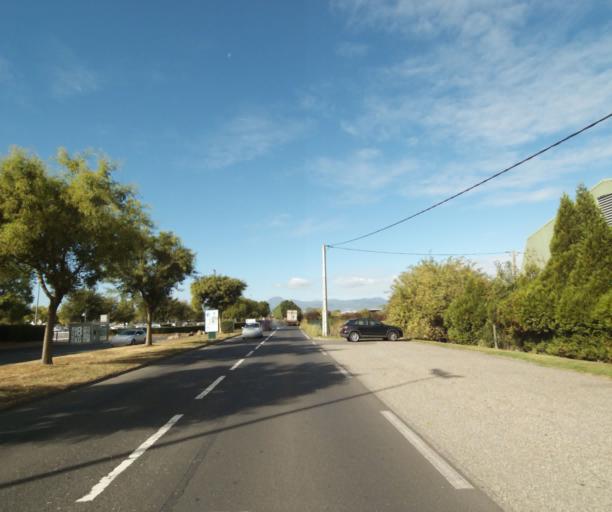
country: FR
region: Auvergne
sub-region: Departement du Puy-de-Dome
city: Malintrat
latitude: 45.7801
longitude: 3.1982
